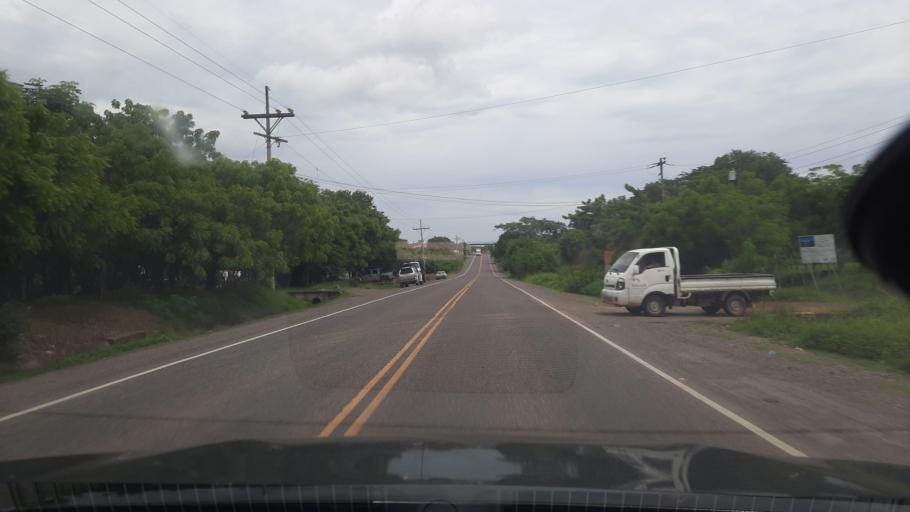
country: HN
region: Valle
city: Jicaro Galan
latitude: 13.5043
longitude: -87.4417
